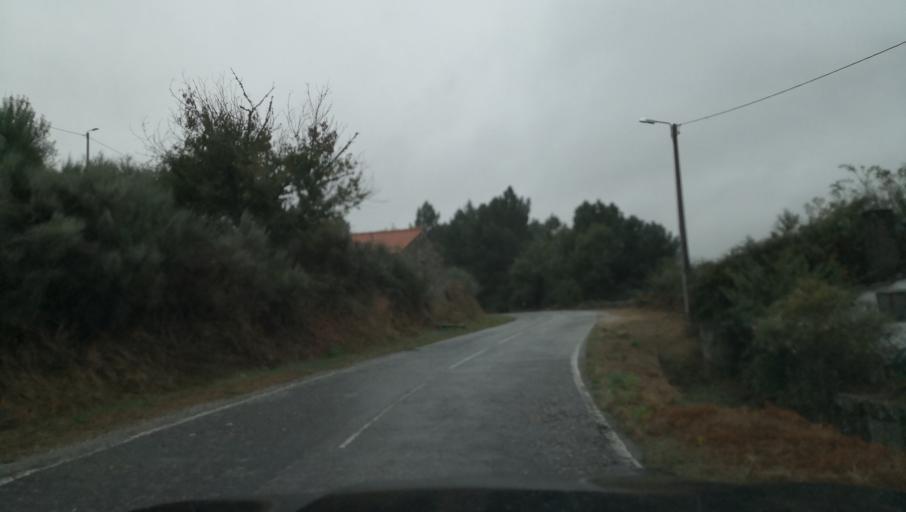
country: PT
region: Vila Real
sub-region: Sabrosa
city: Sabrosa
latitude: 41.3510
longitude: -7.5860
